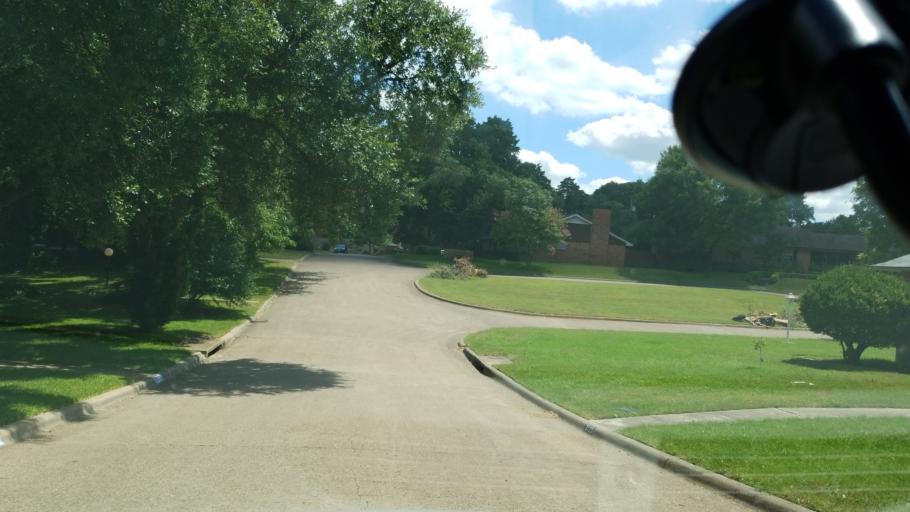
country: US
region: Texas
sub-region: Dallas County
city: Cockrell Hill
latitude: 32.7018
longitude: -96.8728
